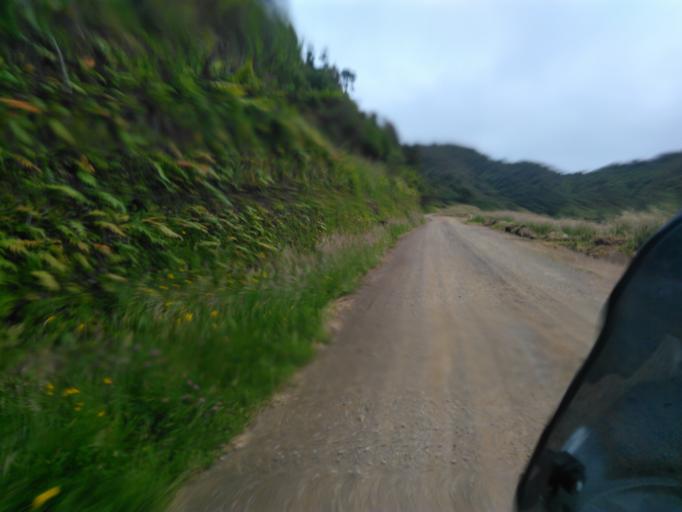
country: NZ
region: Bay of Plenty
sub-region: Opotiki District
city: Opotiki
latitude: -38.0970
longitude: 177.4856
